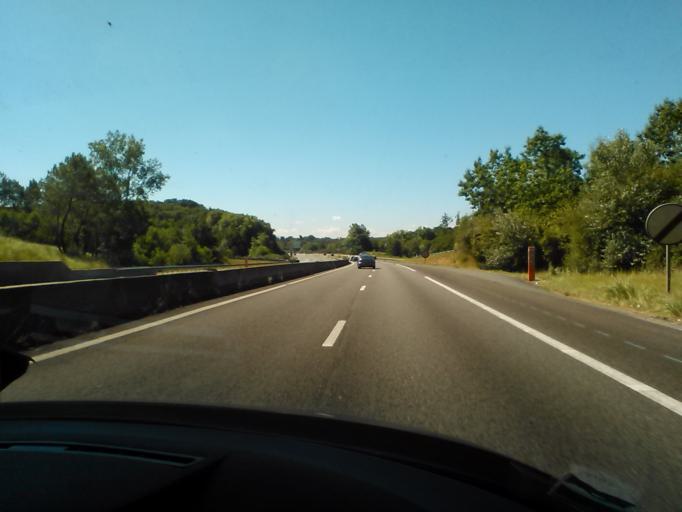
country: FR
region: Aquitaine
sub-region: Departement des Landes
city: Ondres
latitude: 43.5413
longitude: -1.4318
